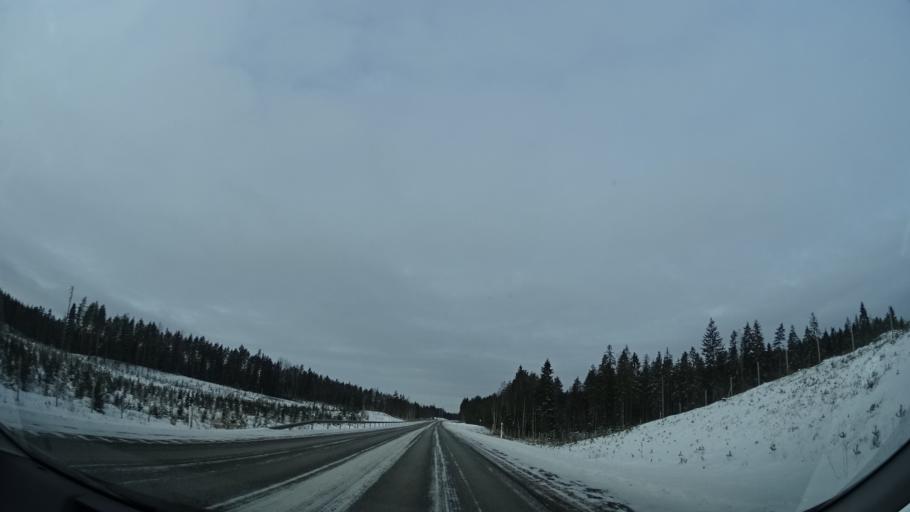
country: FI
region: Uusimaa
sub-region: Helsinki
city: Kaerkoelae
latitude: 60.6094
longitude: 24.0499
